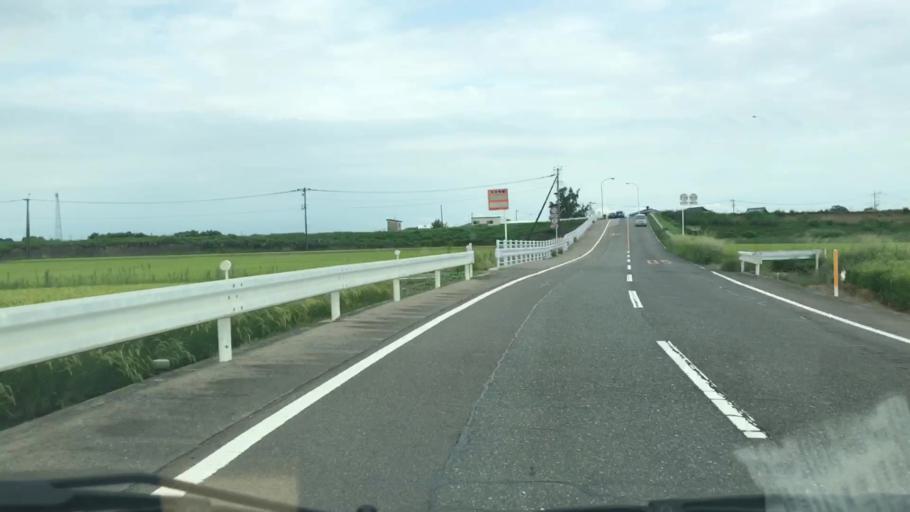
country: JP
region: Saga Prefecture
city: Saga-shi
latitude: 33.2886
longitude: 130.2436
